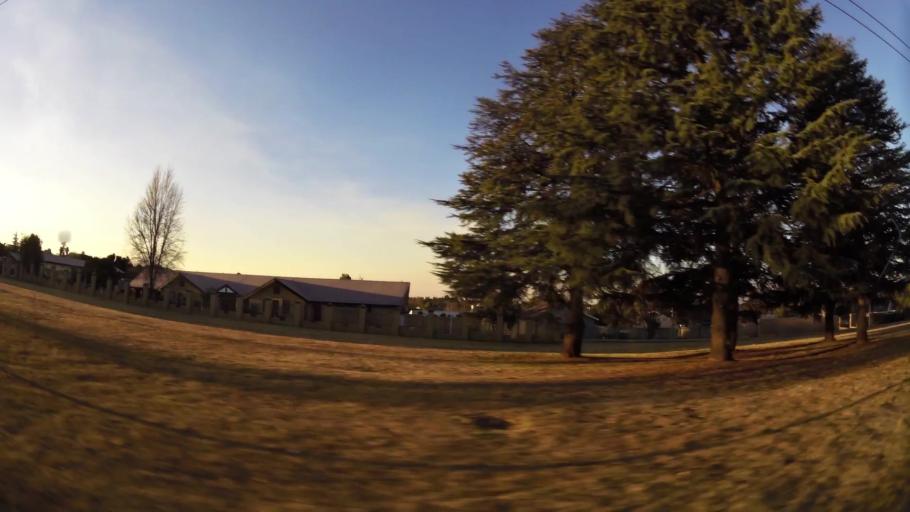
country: ZA
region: Gauteng
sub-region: City of Johannesburg Metropolitan Municipality
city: Roodepoort
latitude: -26.1534
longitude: 27.8944
